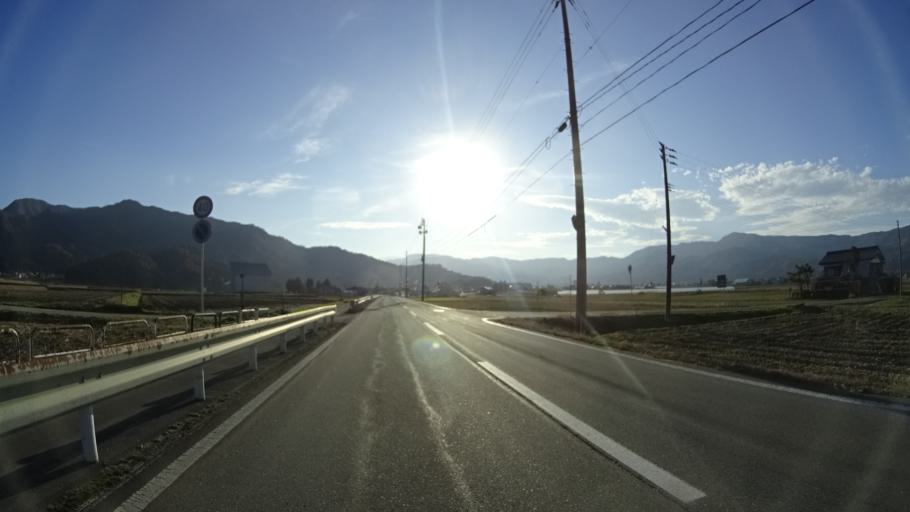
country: JP
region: Niigata
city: Shiozawa
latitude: 37.0139
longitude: 138.8551
